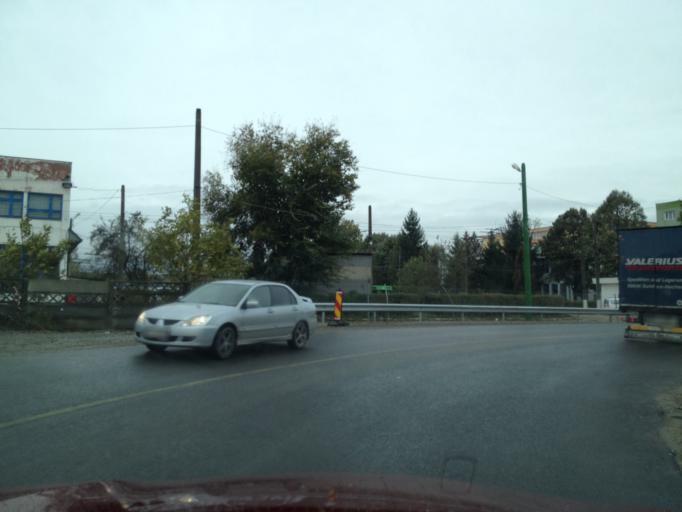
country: RO
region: Brasov
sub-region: Comuna Sanpetru
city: Sanpetru
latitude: 45.6864
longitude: 25.6197
